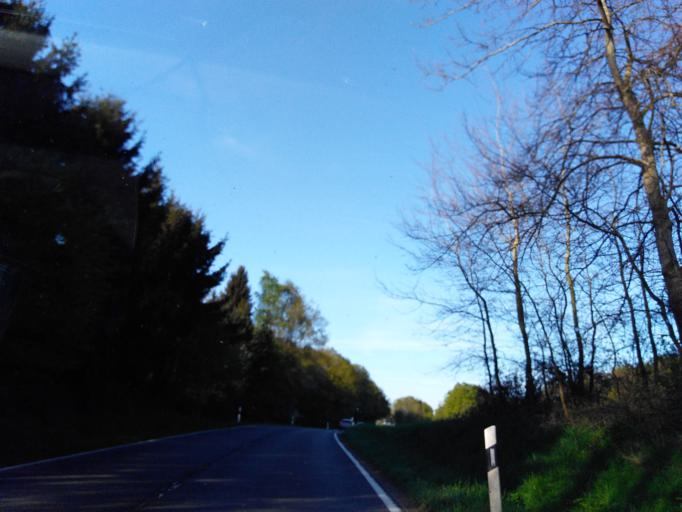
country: DE
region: North Rhine-Westphalia
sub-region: Regierungsbezirk Koln
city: Hennef
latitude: 50.8538
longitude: 7.3006
